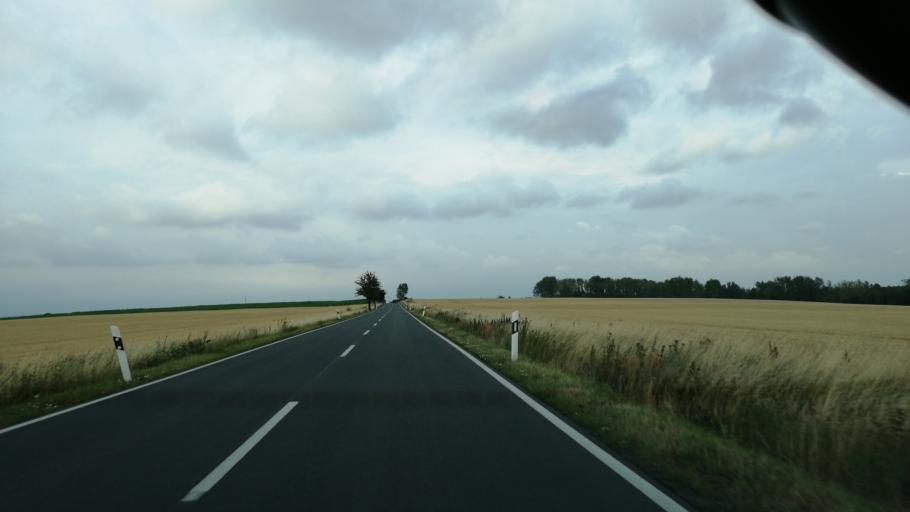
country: DE
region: Saxony-Anhalt
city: Mansfeld
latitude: 51.5728
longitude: 11.4501
